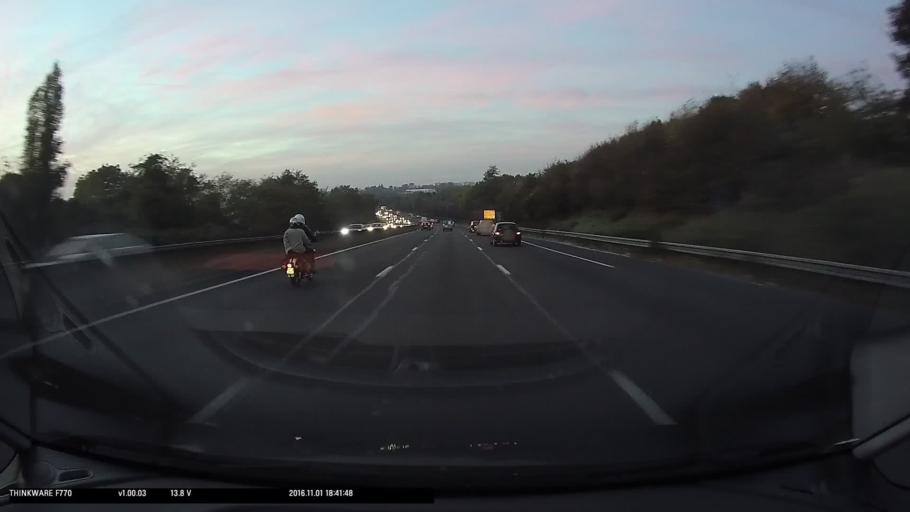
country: FR
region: Ile-de-France
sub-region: Departement de l'Essonne
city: Longjumeau
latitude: 48.6923
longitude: 2.3216
